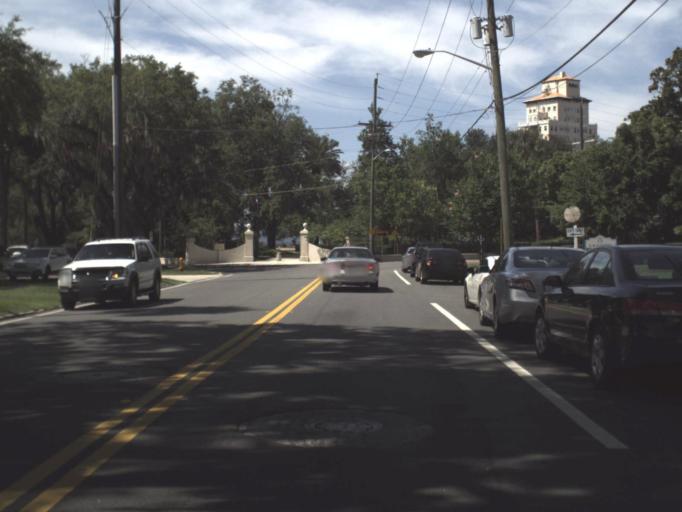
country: US
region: Florida
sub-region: Duval County
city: Jacksonville
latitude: 30.3122
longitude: -81.6786
